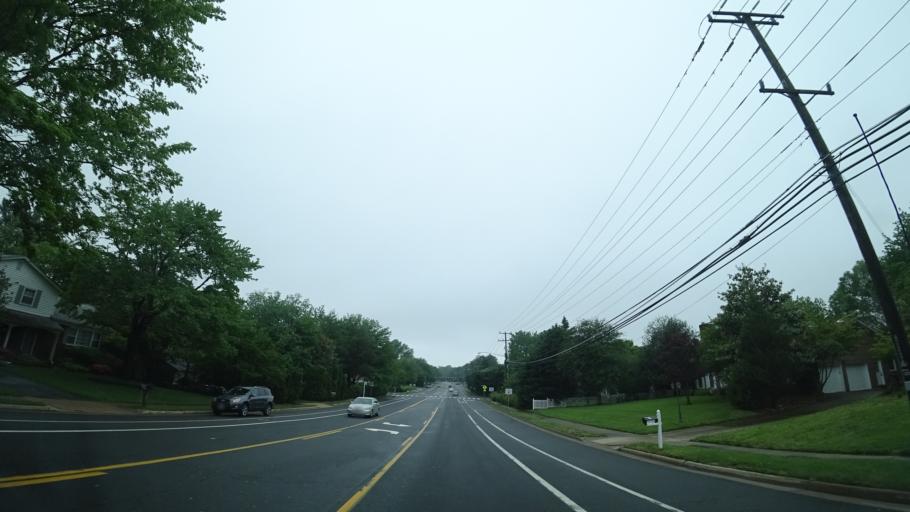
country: US
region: Virginia
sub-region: Fairfax County
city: Tysons Corner
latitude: 38.9415
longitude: -77.2241
